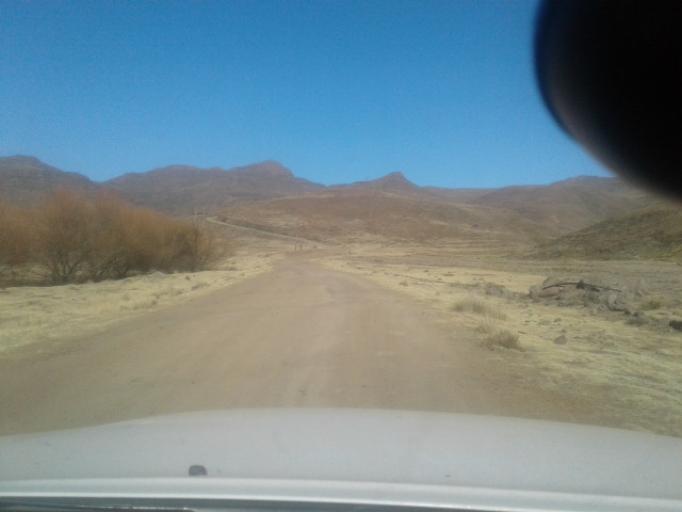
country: LS
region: Maseru
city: Nako
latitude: -29.3844
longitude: 28.0083
